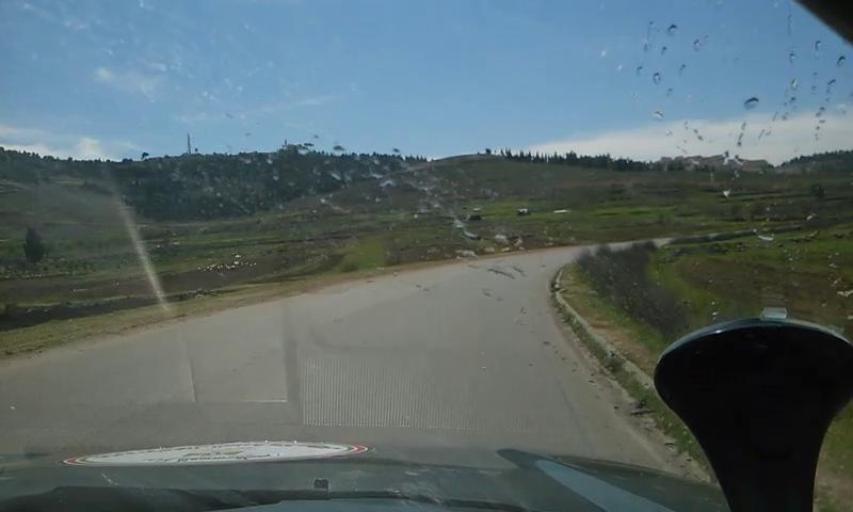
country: PS
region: West Bank
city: Al Jib
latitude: 31.8433
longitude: 35.1777
